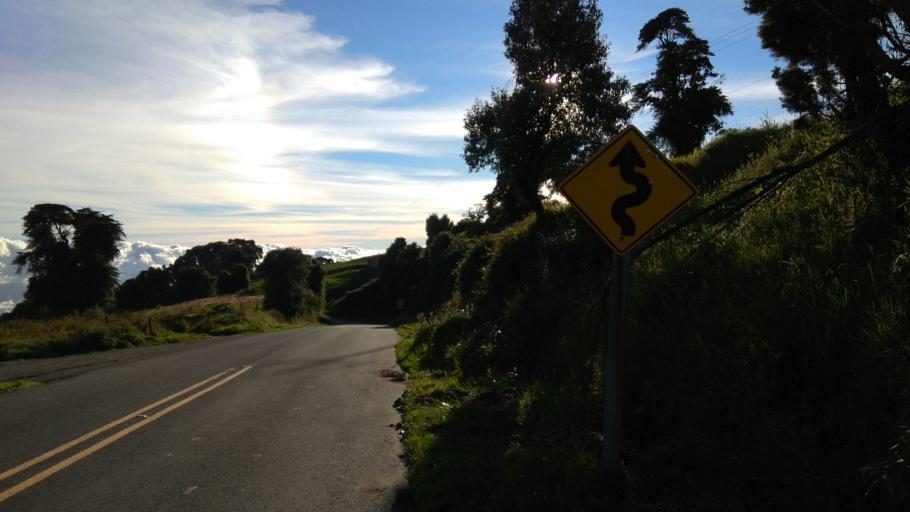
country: CR
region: Cartago
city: Cot
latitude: 9.9690
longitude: -83.8265
